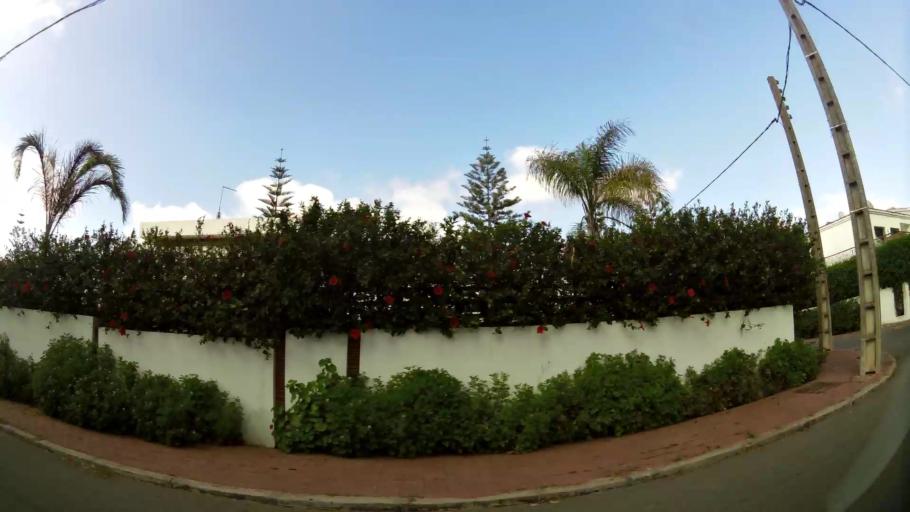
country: MA
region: Rabat-Sale-Zemmour-Zaer
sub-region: Rabat
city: Rabat
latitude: 33.9597
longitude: -6.8531
